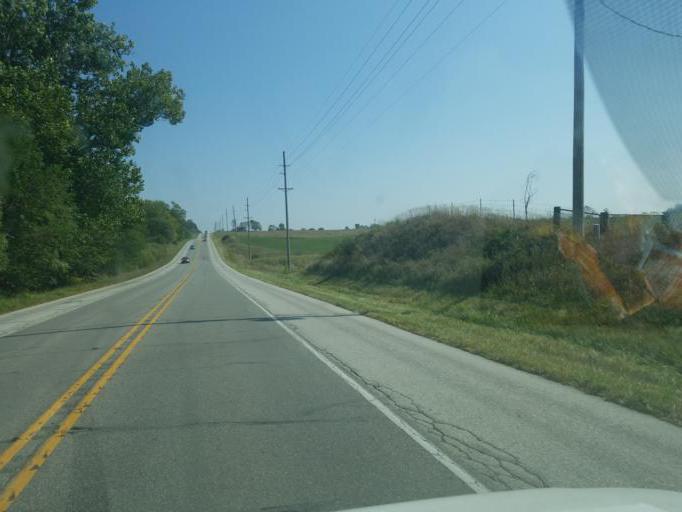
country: US
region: Indiana
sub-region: LaGrange County
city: Lagrange
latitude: 41.6418
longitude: -85.3635
